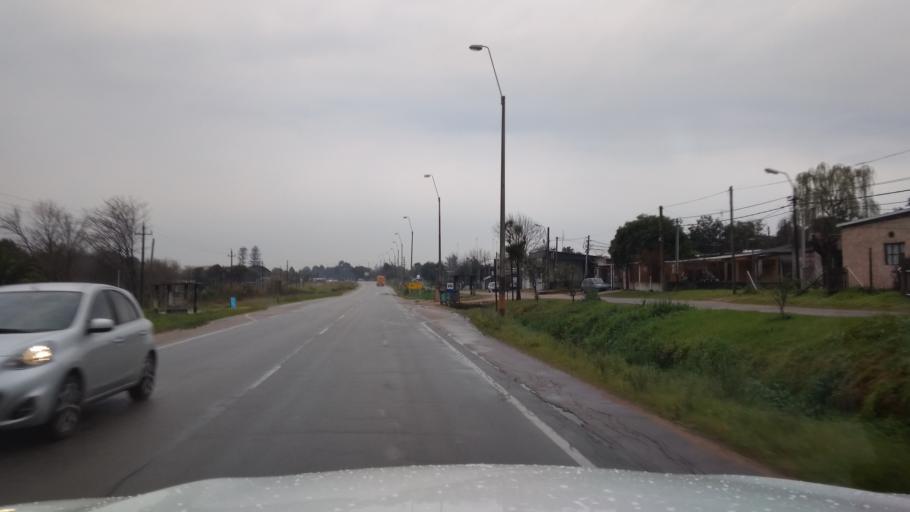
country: UY
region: Canelones
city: Toledo
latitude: -34.7582
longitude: -56.1130
